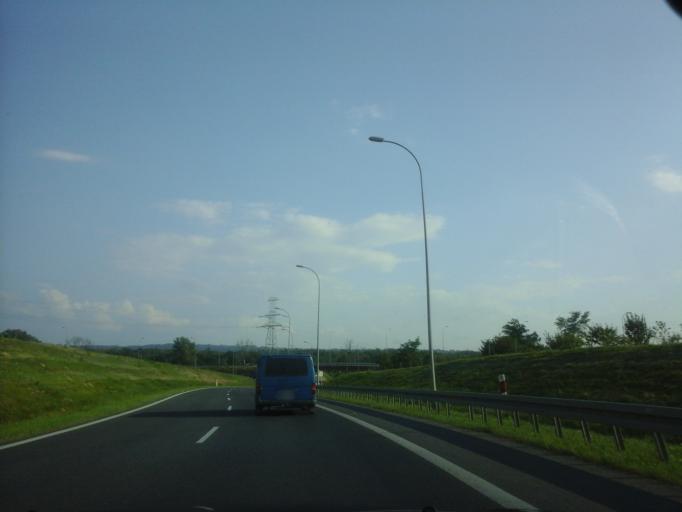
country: PL
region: Lesser Poland Voivodeship
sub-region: Powiat wielicki
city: Czarnochowice
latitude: 50.0126
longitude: 20.0593
